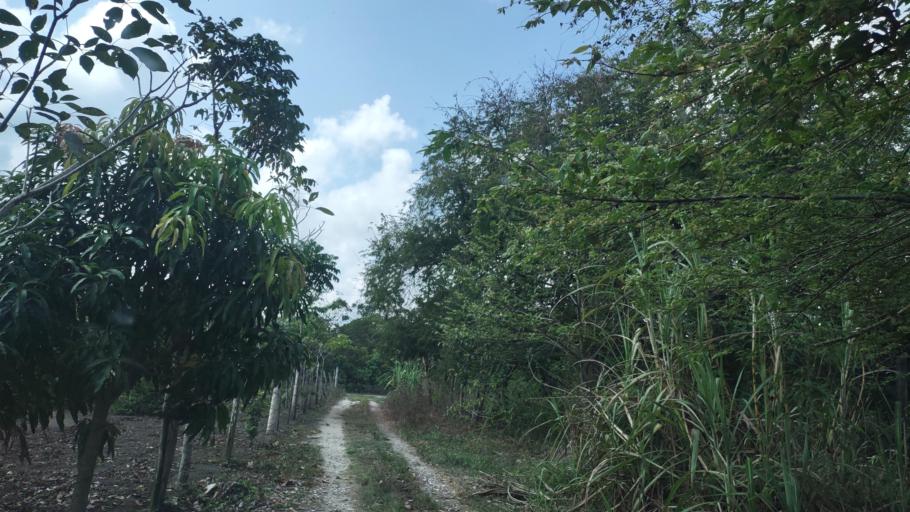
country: MX
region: Veracruz
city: Las Choapas
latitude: 17.9472
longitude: -94.0935
